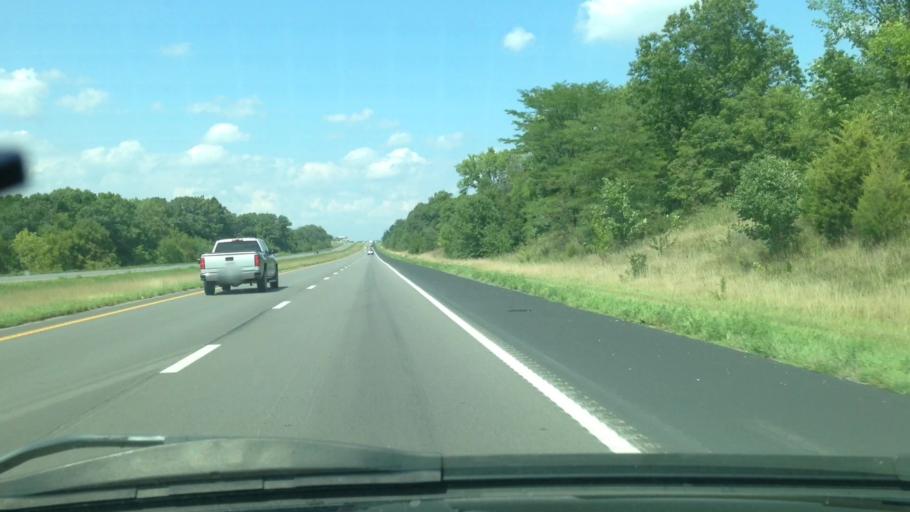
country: US
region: Missouri
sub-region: Lincoln County
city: Troy
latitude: 39.0538
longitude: -90.9737
